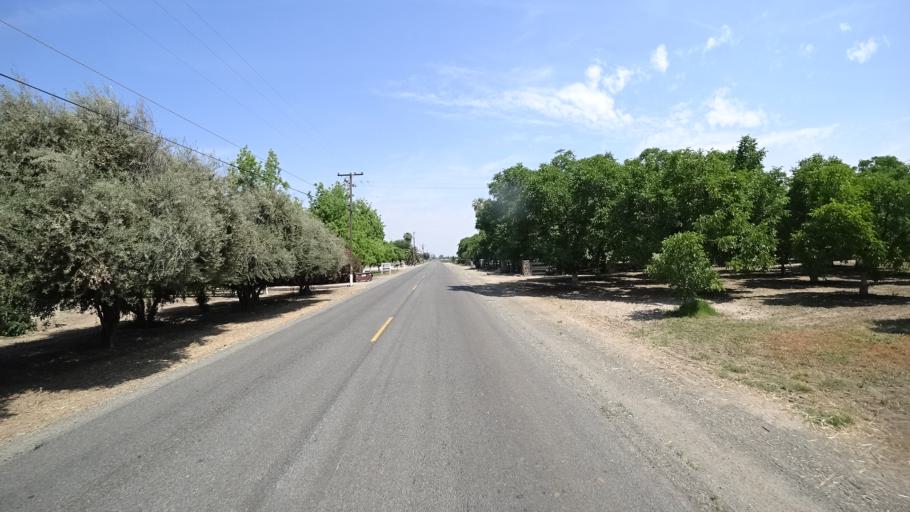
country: US
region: California
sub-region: Kings County
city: Lemoore
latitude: 36.3189
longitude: -119.7628
